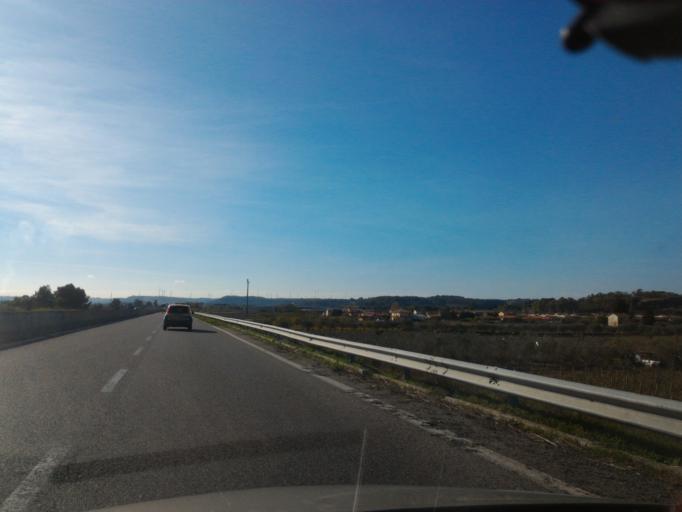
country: IT
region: Calabria
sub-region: Provincia di Crotone
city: Crotone
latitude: 39.1442
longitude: 17.0960
